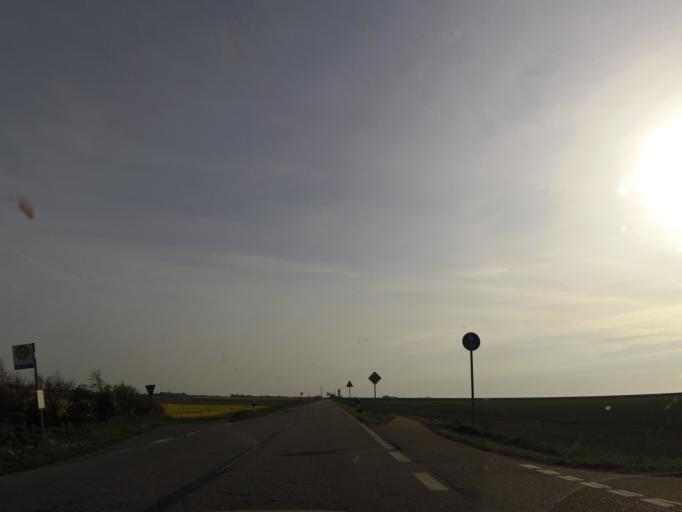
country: DE
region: Schleswig-Holstein
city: Galmsbull
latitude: 54.7463
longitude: 8.7348
